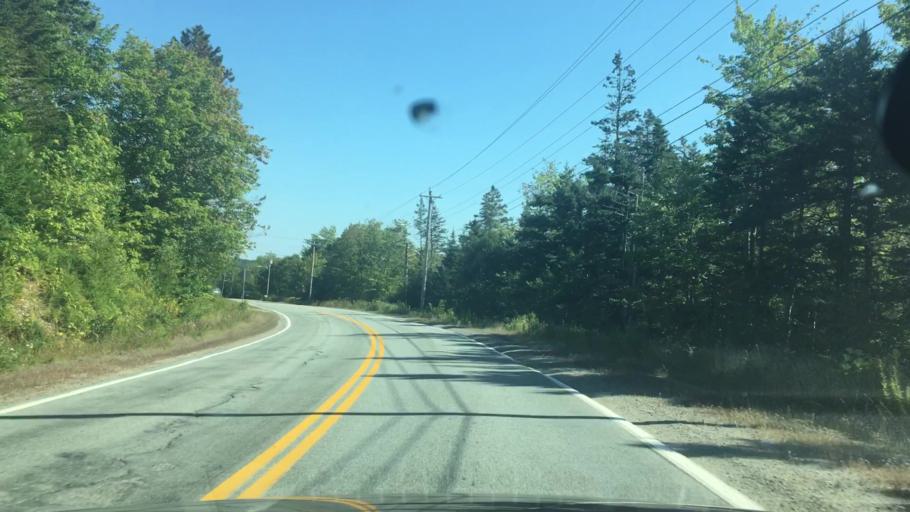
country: CA
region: Nova Scotia
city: New Glasgow
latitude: 44.9107
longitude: -62.5430
